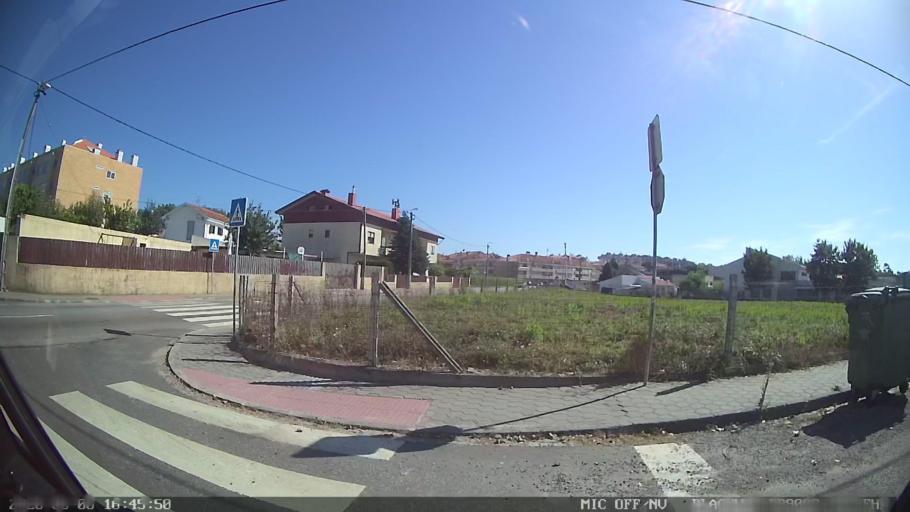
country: PT
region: Porto
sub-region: Vila Nova de Gaia
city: Canelas
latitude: 41.0868
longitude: -8.6029
